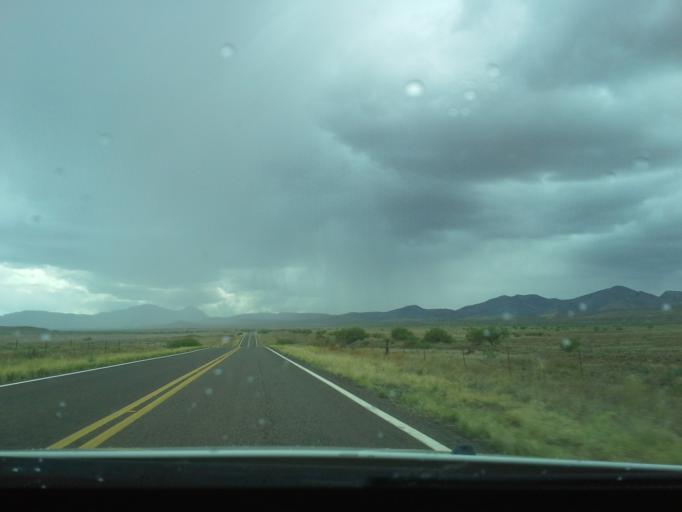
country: US
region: Arizona
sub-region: Cochise County
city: Douglas
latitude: 31.5505
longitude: -109.2735
